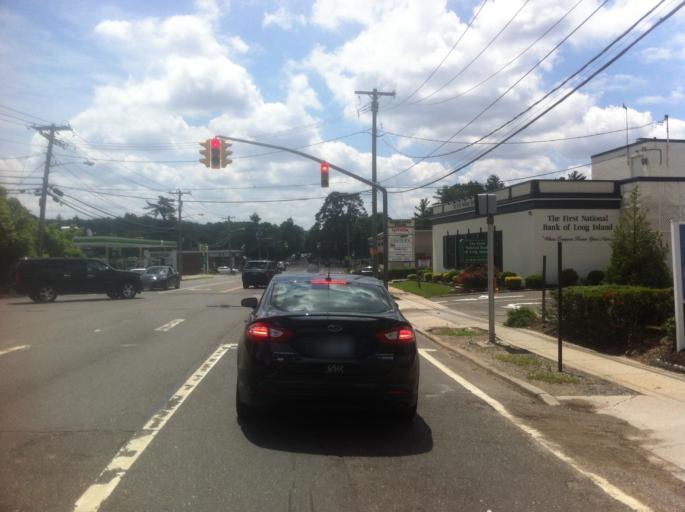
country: US
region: New York
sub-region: Nassau County
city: Greenvale
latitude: 40.8086
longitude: -73.6276
